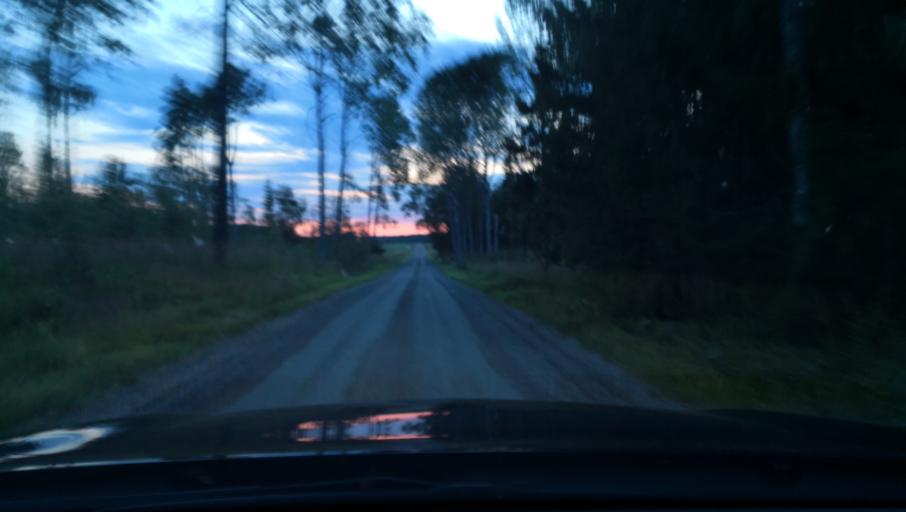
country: SE
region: Uppsala
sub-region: Osthammars Kommun
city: Bjorklinge
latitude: 60.0059
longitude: 17.3353
